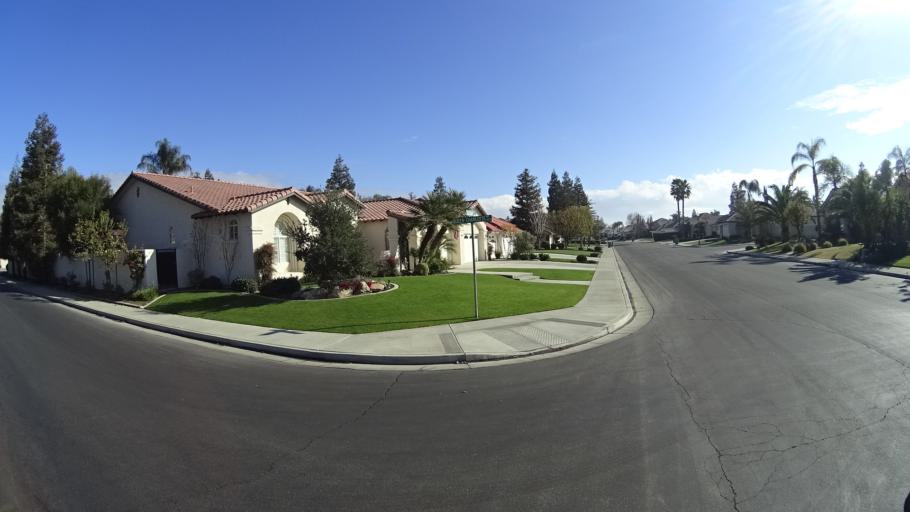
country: US
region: California
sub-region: Kern County
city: Greenacres
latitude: 35.3438
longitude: -119.1183
